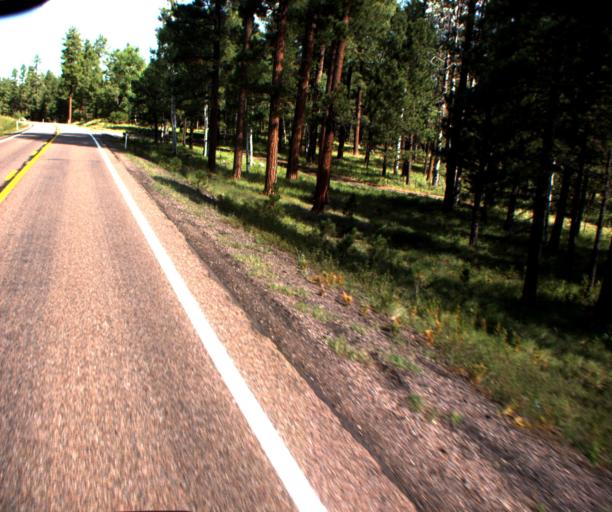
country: US
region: Arizona
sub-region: Navajo County
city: Pinetop-Lakeside
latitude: 34.0333
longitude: -109.6620
